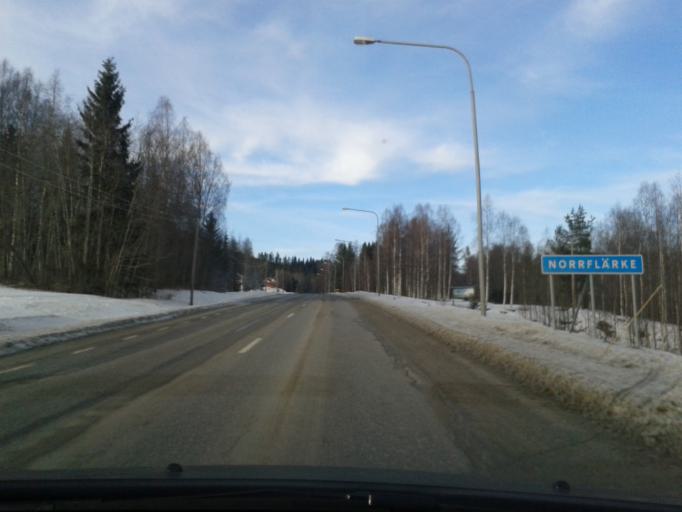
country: SE
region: Vaesternorrland
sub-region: OErnskoeldsviks Kommun
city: Bredbyn
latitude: 63.4883
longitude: 18.0840
